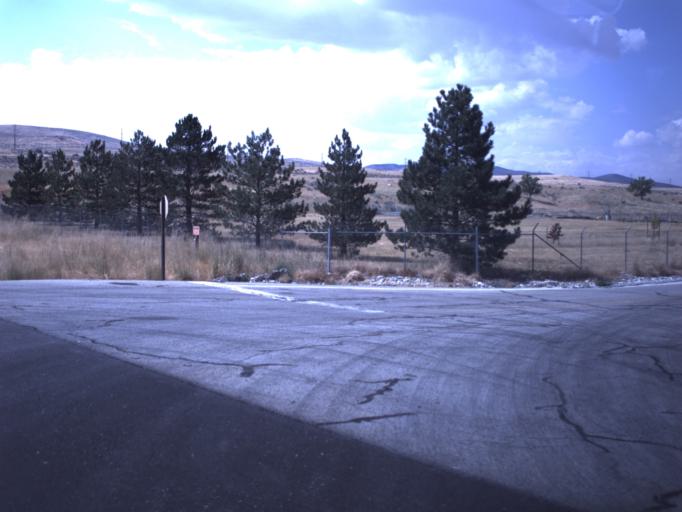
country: US
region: Utah
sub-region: Box Elder County
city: Garland
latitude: 41.7847
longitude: -112.1646
